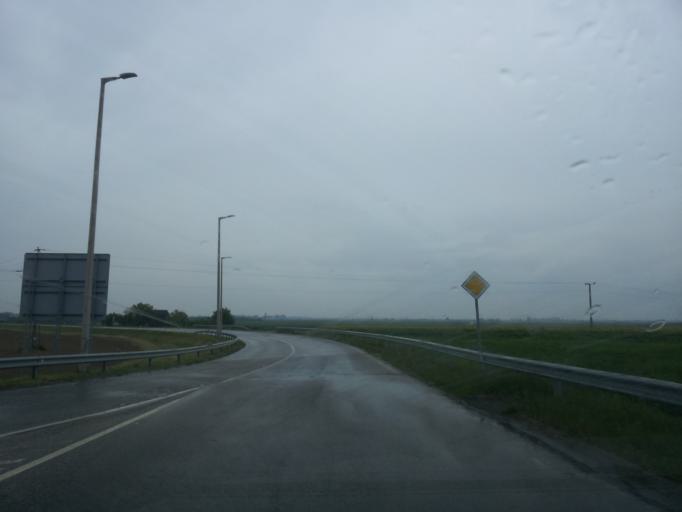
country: HU
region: Tolna
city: Szekszard
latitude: 46.3087
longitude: 18.6948
